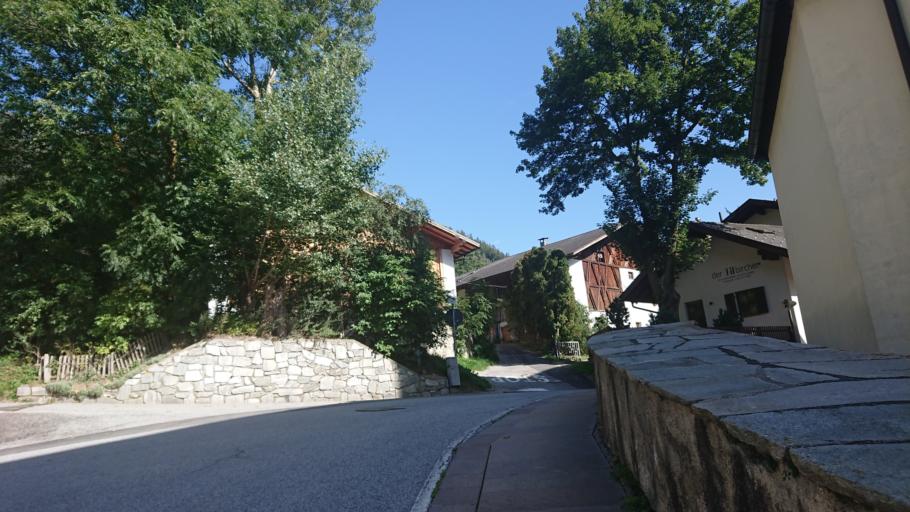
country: IT
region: Trentino-Alto Adige
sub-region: Bolzano
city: Campo di Trens
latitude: 46.8769
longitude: 11.4848
